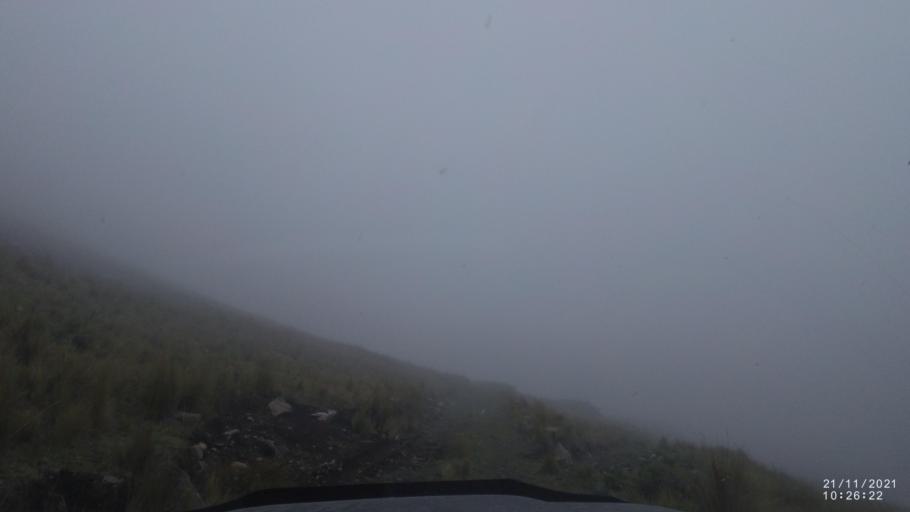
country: BO
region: Cochabamba
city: Cochabamba
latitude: -16.9747
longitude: -66.2660
